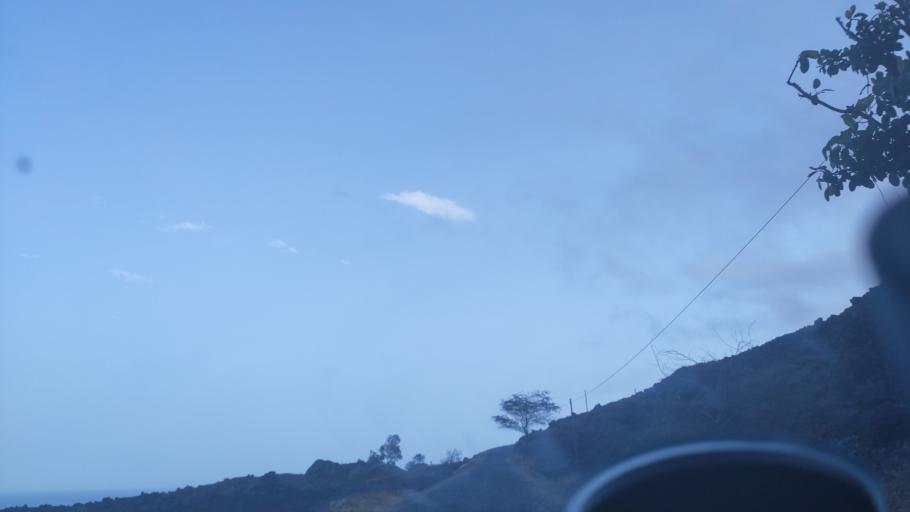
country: CV
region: Mosteiros
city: Porto dos Mosteiros
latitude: 15.0118
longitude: -24.3073
